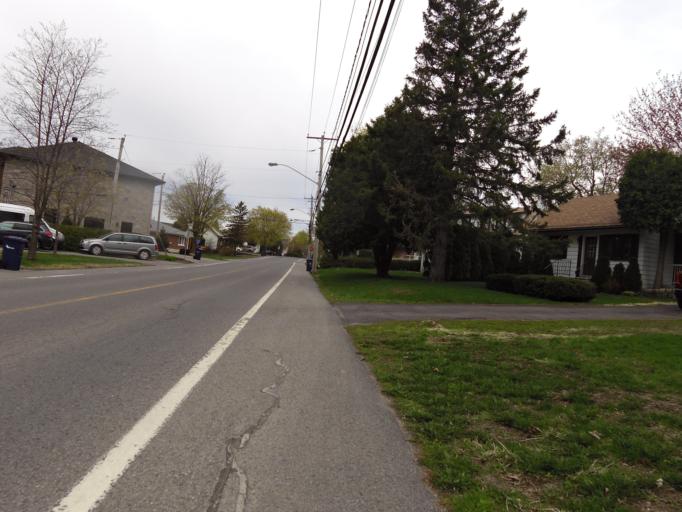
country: CA
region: Quebec
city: Dollard-Des Ormeaux
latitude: 45.5207
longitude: -73.8213
